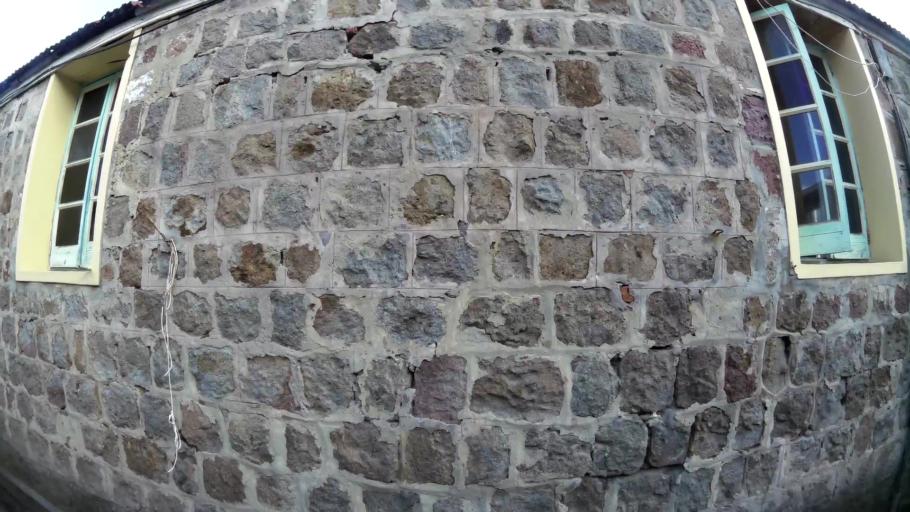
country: KN
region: Saint Paul Charlestown
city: Charlestown
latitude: 17.1385
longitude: -62.6291
